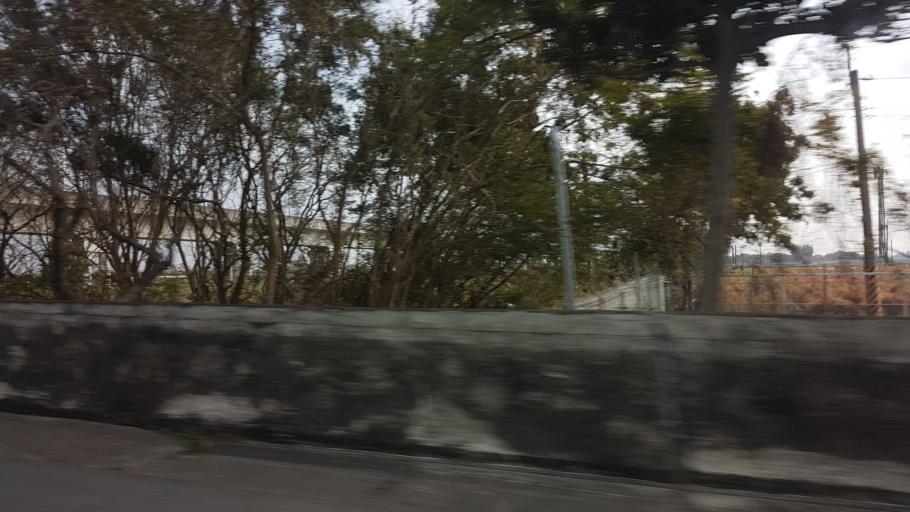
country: TW
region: Taiwan
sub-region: Chiayi
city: Taibao
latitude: 23.4287
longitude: 120.3214
